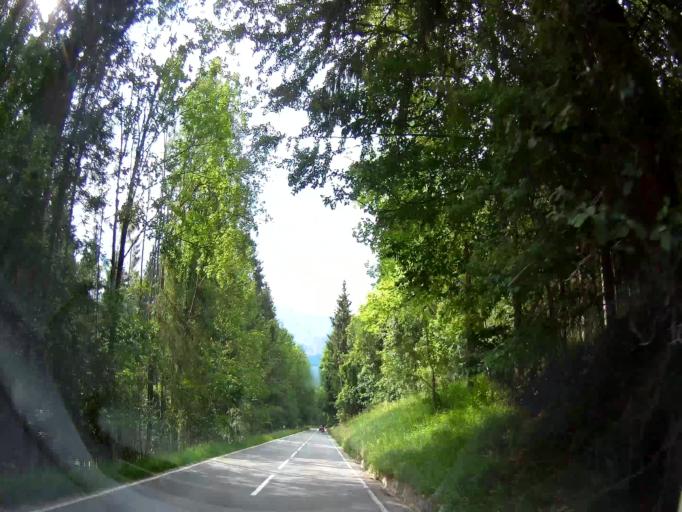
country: DE
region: Bavaria
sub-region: Upper Bavaria
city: Marktschellenberg
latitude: 47.6447
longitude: 13.0601
